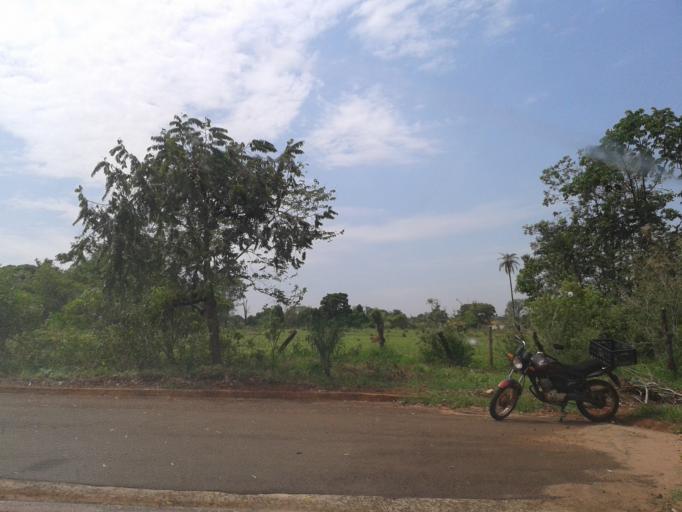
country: BR
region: Minas Gerais
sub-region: Ituiutaba
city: Ituiutaba
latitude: -18.9875
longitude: -49.4399
